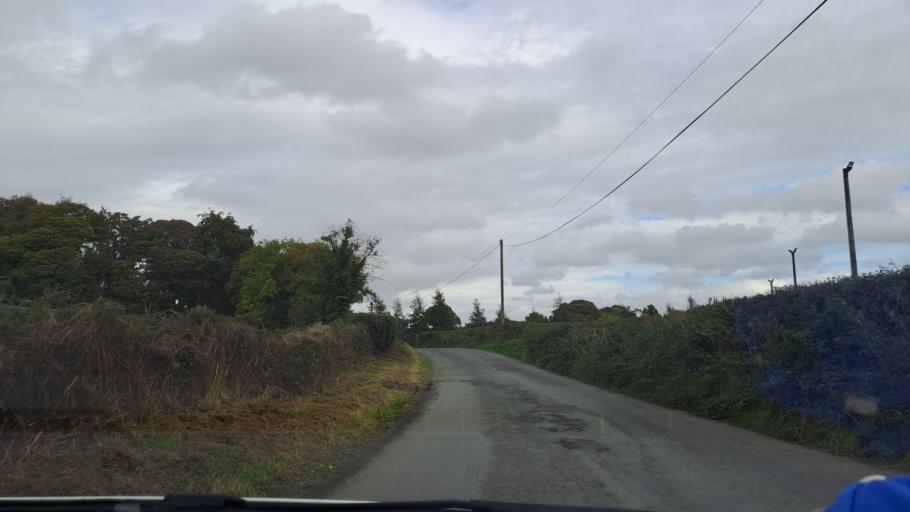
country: IE
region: Ulster
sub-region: An Cabhan
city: Kingscourt
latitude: 53.9398
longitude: -6.7888
